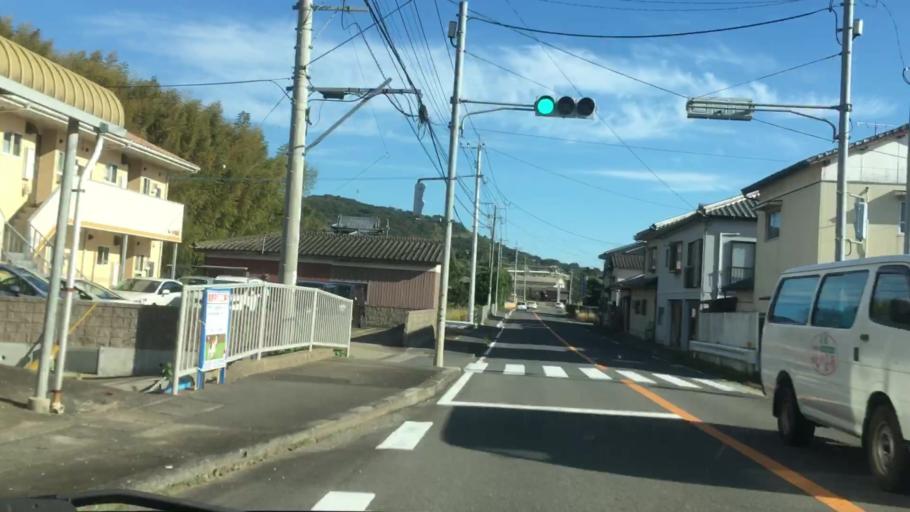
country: JP
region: Nagasaki
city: Sasebo
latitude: 33.0207
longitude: 129.7368
